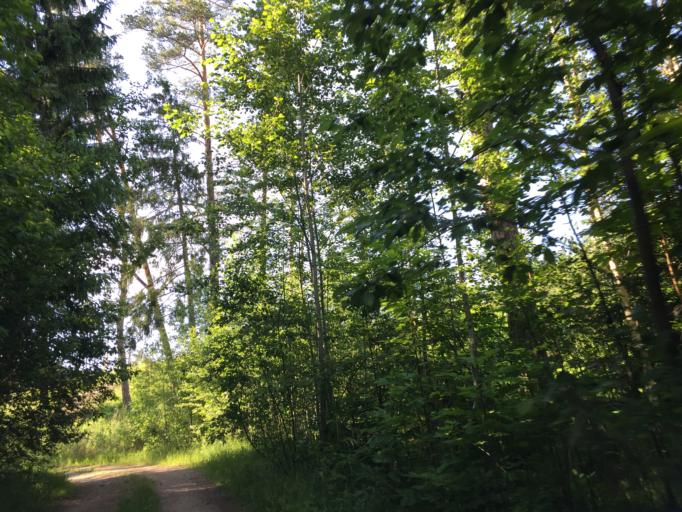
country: LV
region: Tukuma Rajons
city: Tukums
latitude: 57.0322
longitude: 23.2199
